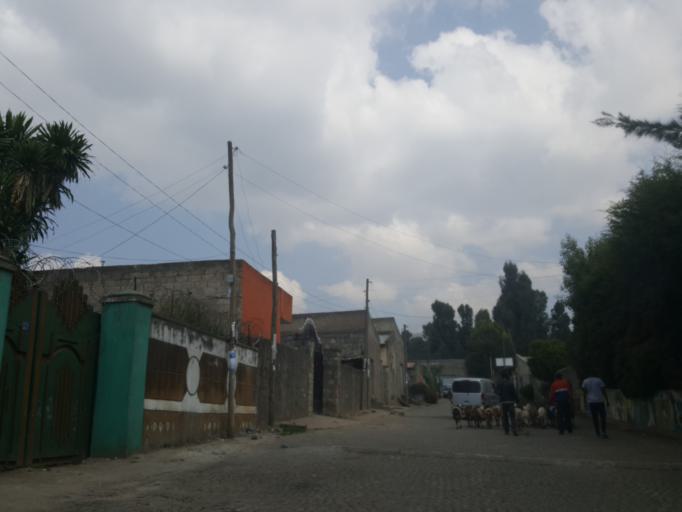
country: ET
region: Adis Abeba
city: Addis Ababa
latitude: 9.0616
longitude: 38.7208
